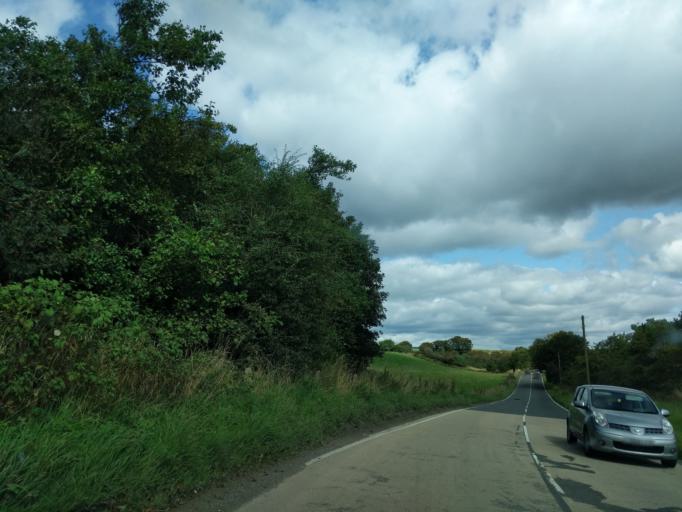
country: GB
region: Scotland
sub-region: Fife
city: Dunfermline
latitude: 56.0983
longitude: -3.4667
